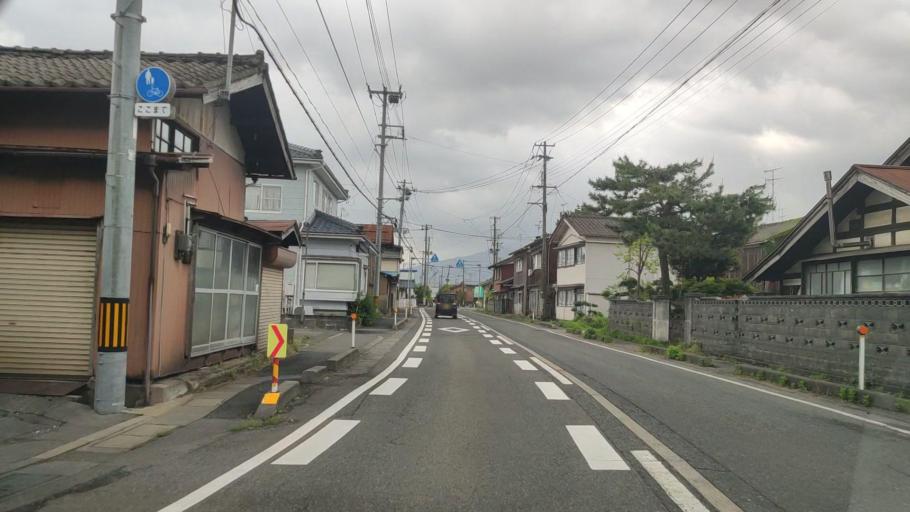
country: JP
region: Niigata
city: Gosen
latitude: 37.7367
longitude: 139.1857
